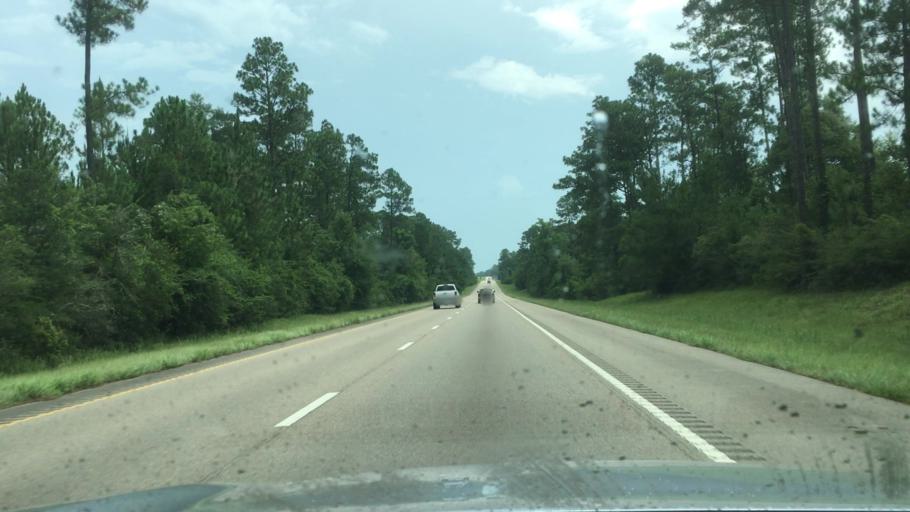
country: US
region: Mississippi
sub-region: Lamar County
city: Lumberton
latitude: 30.9109
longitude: -89.4660
